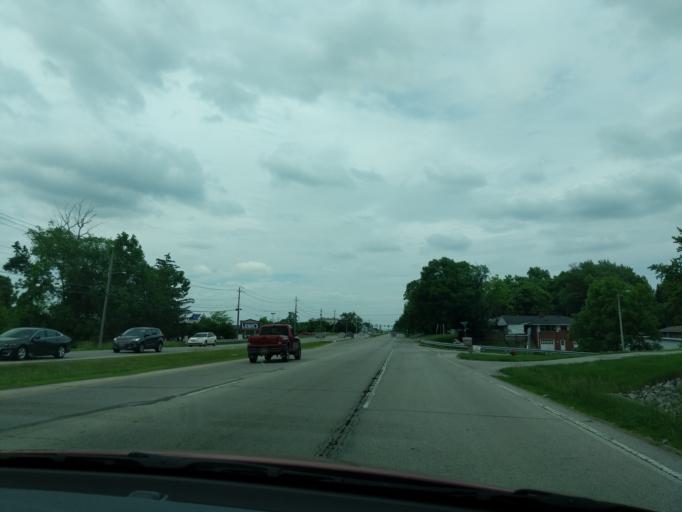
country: US
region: Indiana
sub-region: Madison County
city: Anderson
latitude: 40.0790
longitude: -85.6527
